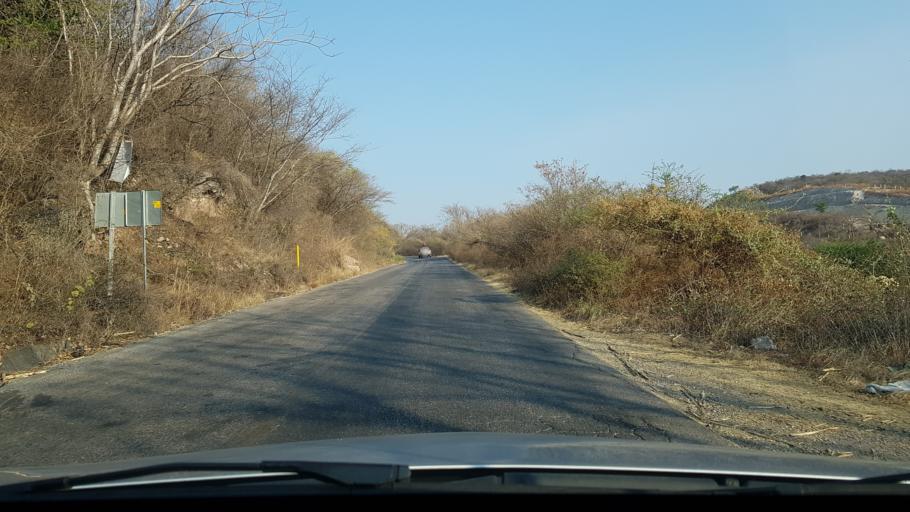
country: MX
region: Morelos
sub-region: Tepalcingo
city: Zacapalco
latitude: 18.6565
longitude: -99.0397
